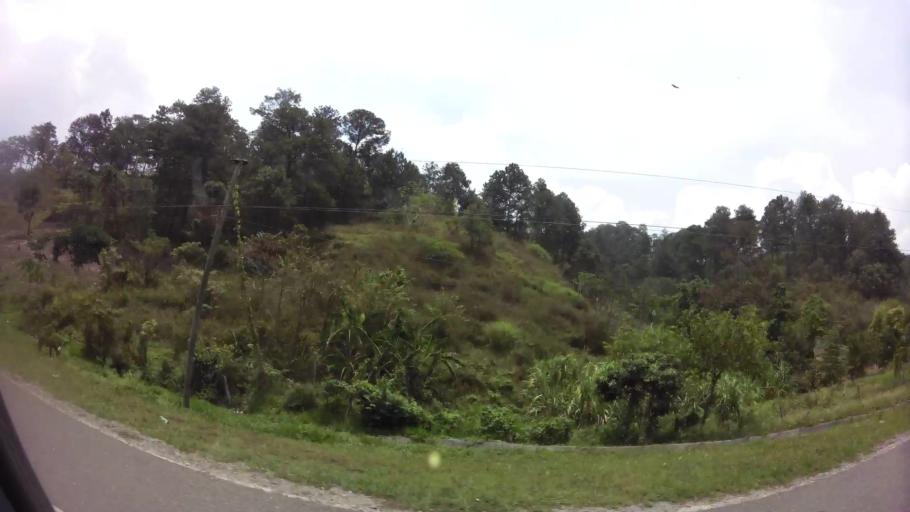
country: HN
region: Comayagua
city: Taulabe
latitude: 14.6814
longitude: -87.9554
